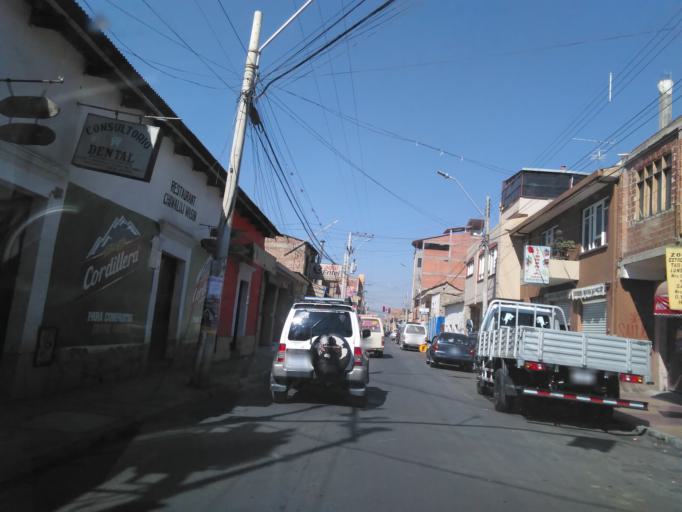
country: BO
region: Cochabamba
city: Sipe Sipe
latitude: -17.3978
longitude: -66.2792
